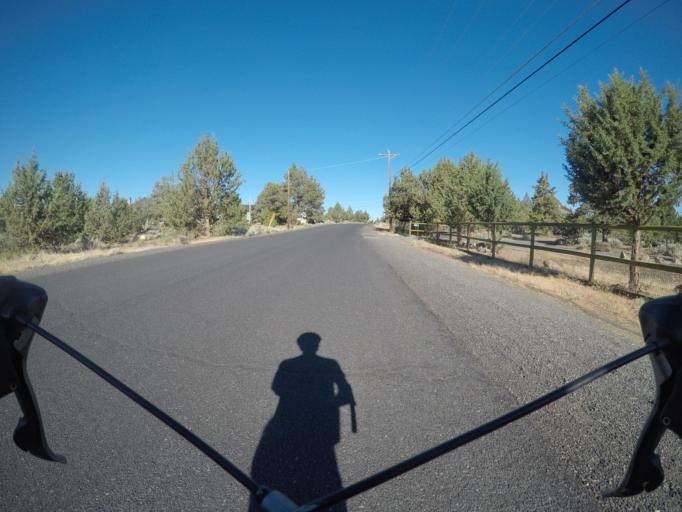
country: US
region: Oregon
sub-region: Deschutes County
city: Bend
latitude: 44.1727
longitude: -121.2674
